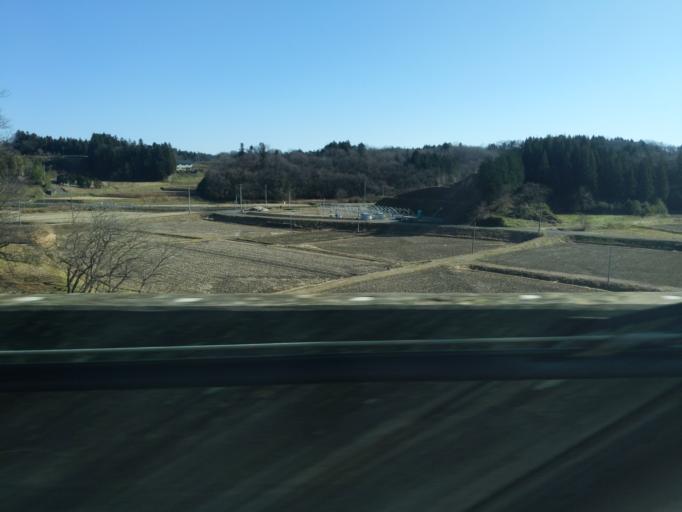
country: JP
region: Fukushima
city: Nihommatsu
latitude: 37.5531
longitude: 140.4521
